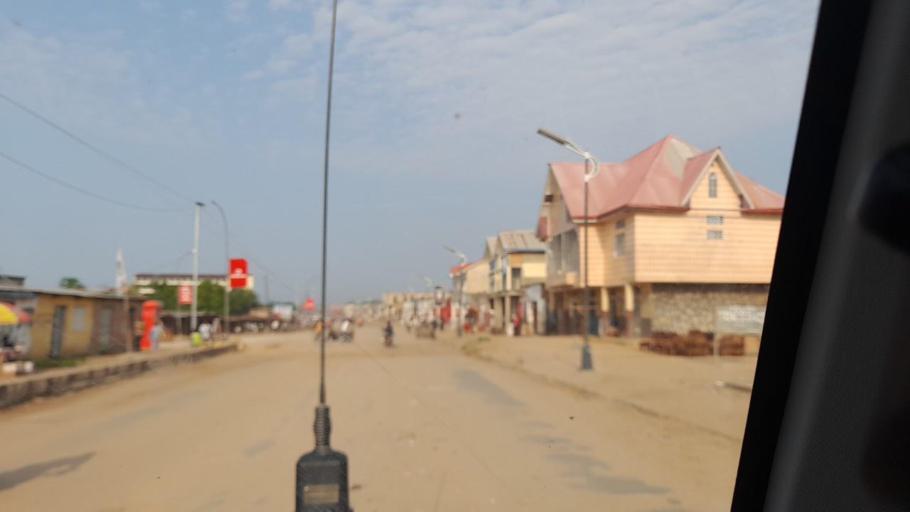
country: CD
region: Kasai-Occidental
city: Kananga
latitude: -5.8941
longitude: 22.4040
